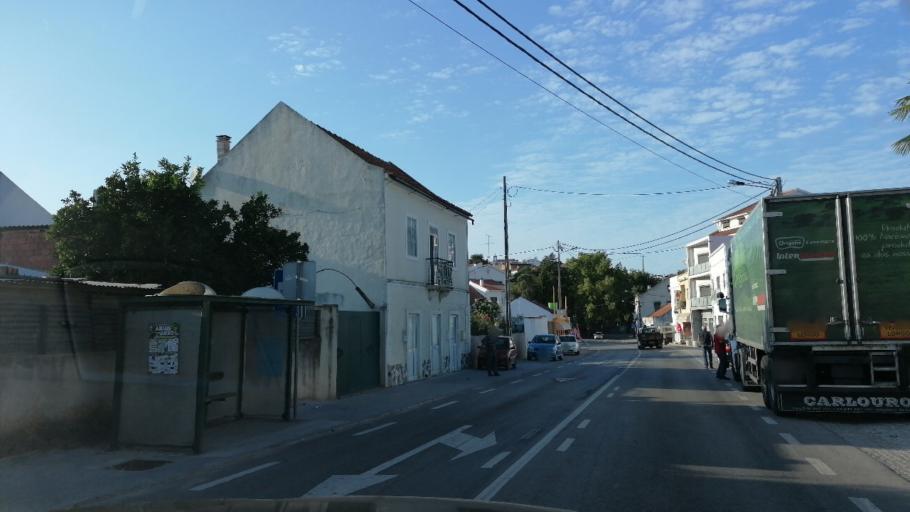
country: PT
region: Santarem
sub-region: Alcanena
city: Alcanena
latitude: 39.3790
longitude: -8.6608
